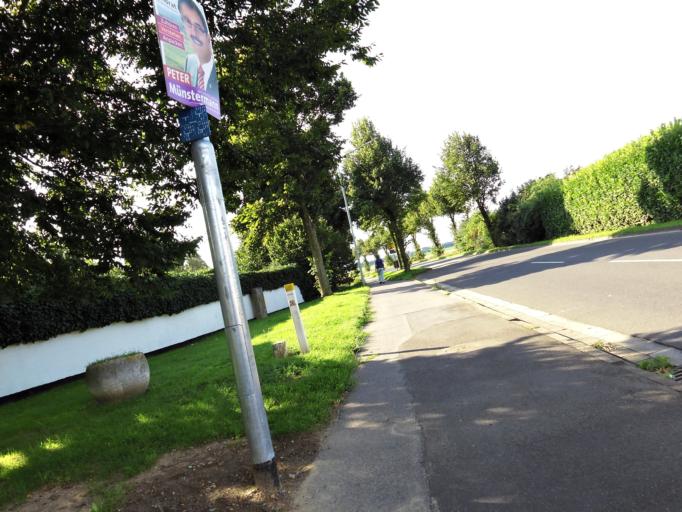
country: DE
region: North Rhine-Westphalia
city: Siersdorf
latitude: 50.8950
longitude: 6.2292
